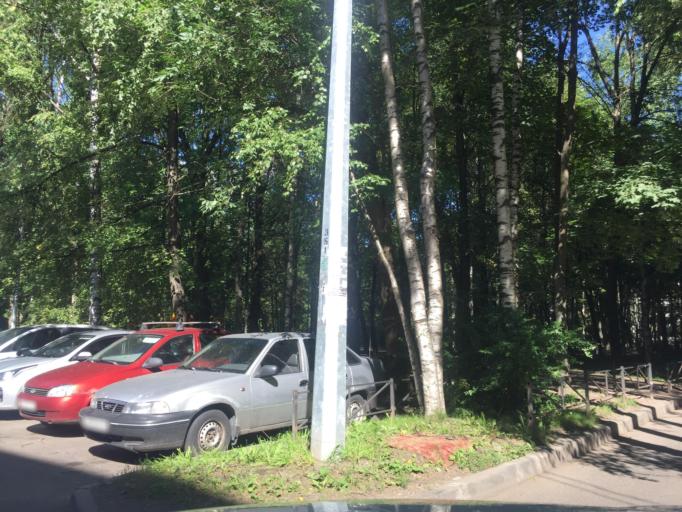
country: RU
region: Leningrad
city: Kalininskiy
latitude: 60.0038
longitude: 30.3951
